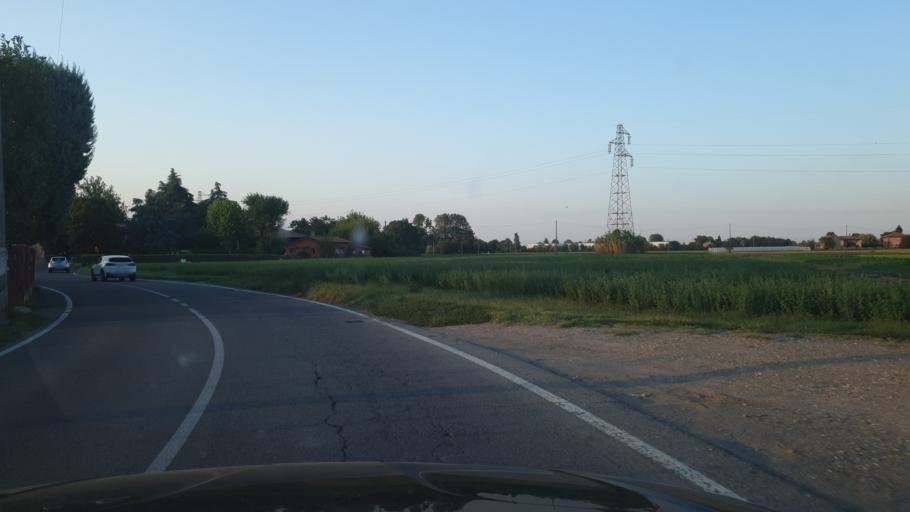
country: IT
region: Emilia-Romagna
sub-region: Provincia di Bologna
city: Quarto Inferiore
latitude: 44.5220
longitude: 11.3812
